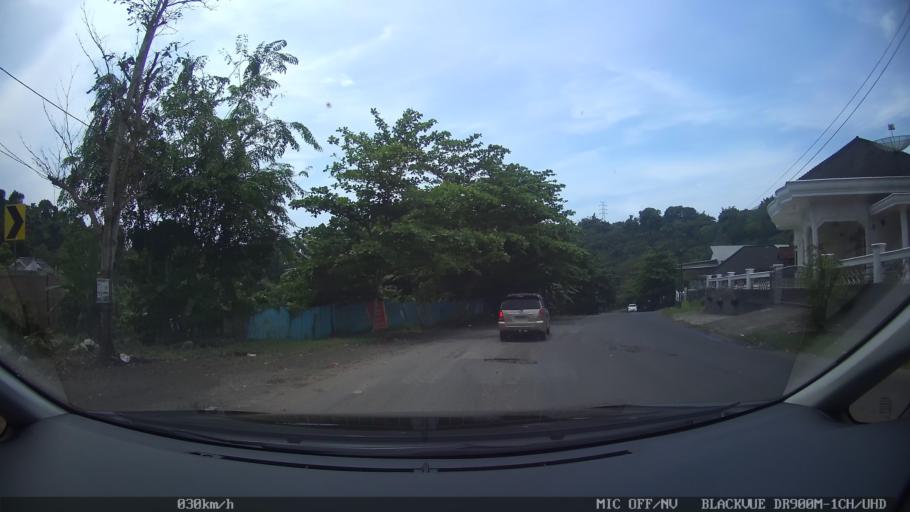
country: ID
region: Lampung
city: Bandarlampung
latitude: -5.4376
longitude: 105.2447
